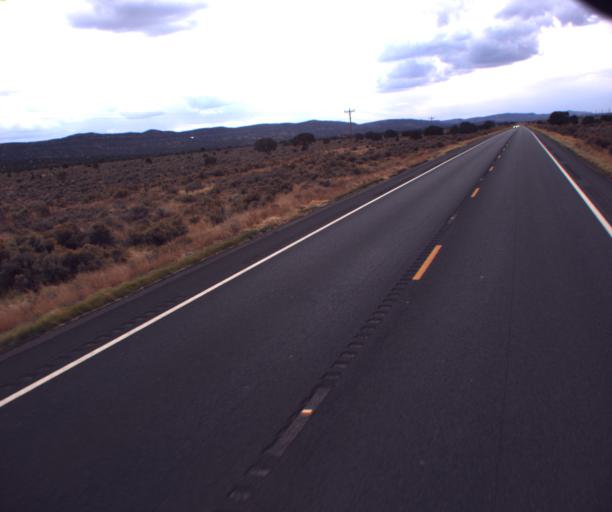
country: US
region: Arizona
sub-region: Navajo County
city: Kayenta
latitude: 36.5115
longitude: -110.6015
